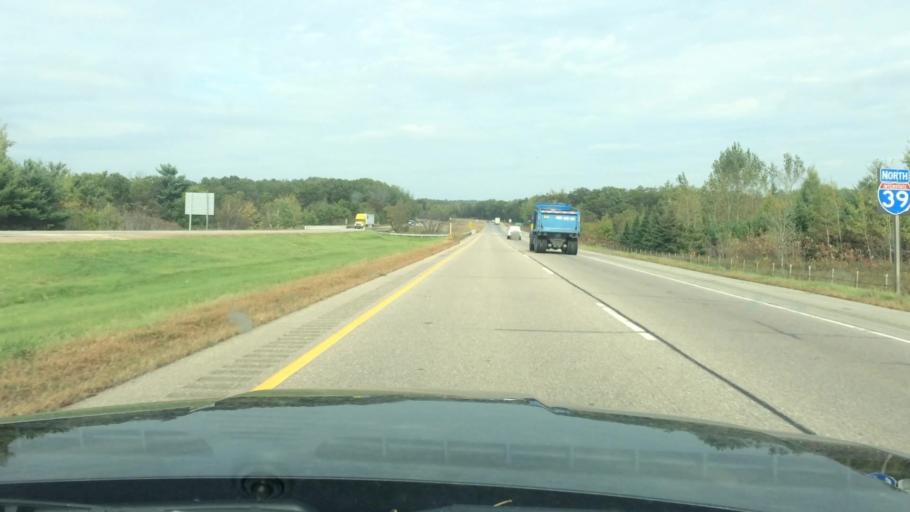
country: US
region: Wisconsin
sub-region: Marathon County
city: Mosinee
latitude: 44.6820
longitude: -89.6412
